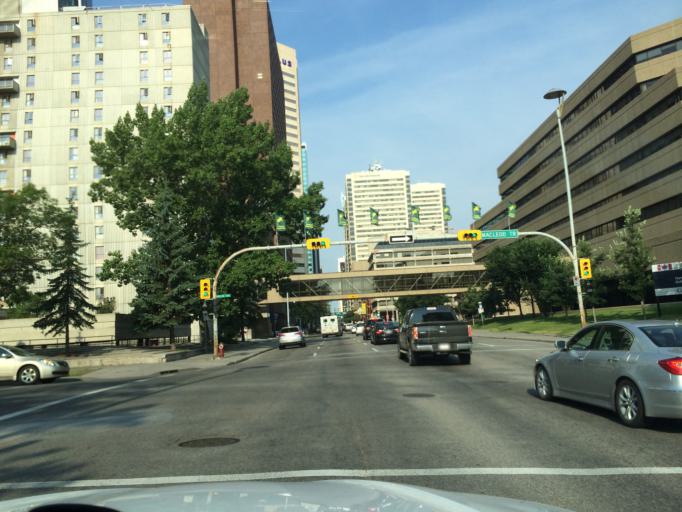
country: CA
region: Alberta
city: Calgary
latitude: 51.0492
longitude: -114.0576
